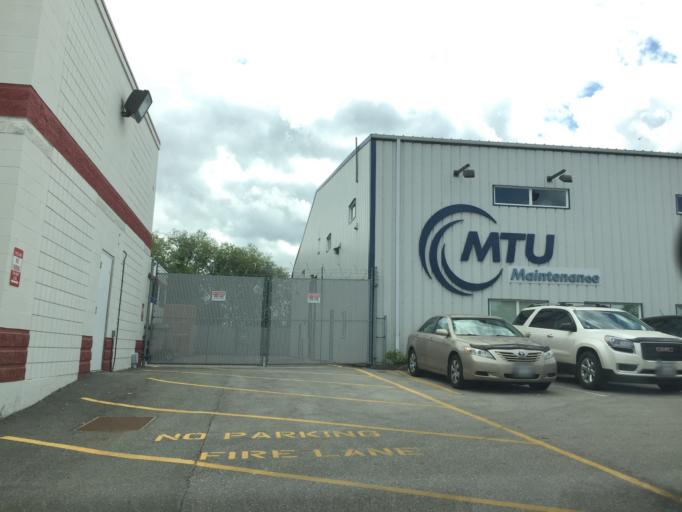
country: CA
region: British Columbia
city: Richmond
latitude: 49.1795
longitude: -123.1518
